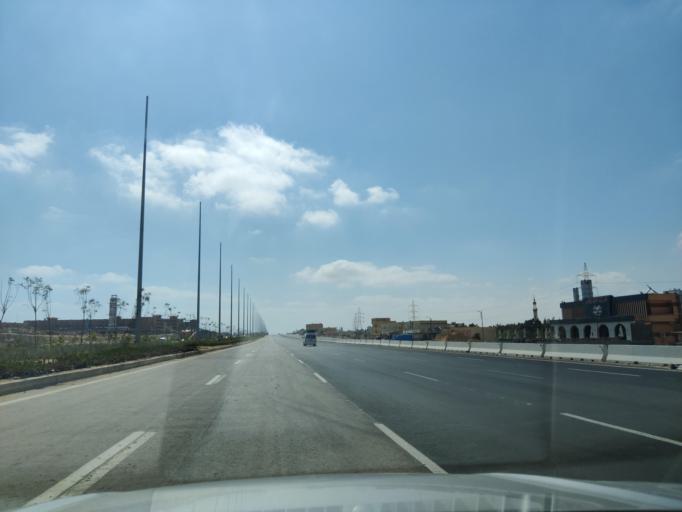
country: EG
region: Muhafazat Matruh
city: Al `Alamayn
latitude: 30.9937
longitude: 28.6645
